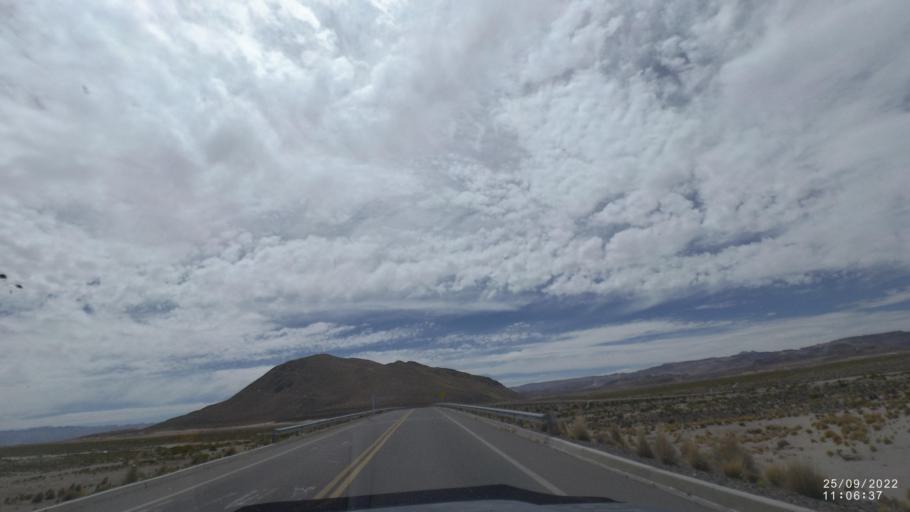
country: BO
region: Oruro
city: Challapata
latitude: -19.3552
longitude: -66.8608
